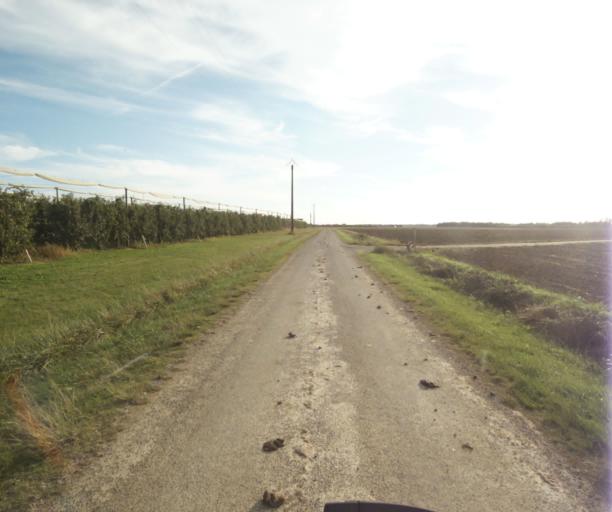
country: FR
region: Midi-Pyrenees
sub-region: Departement du Tarn-et-Garonne
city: Finhan
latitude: 43.9191
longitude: 1.1334
